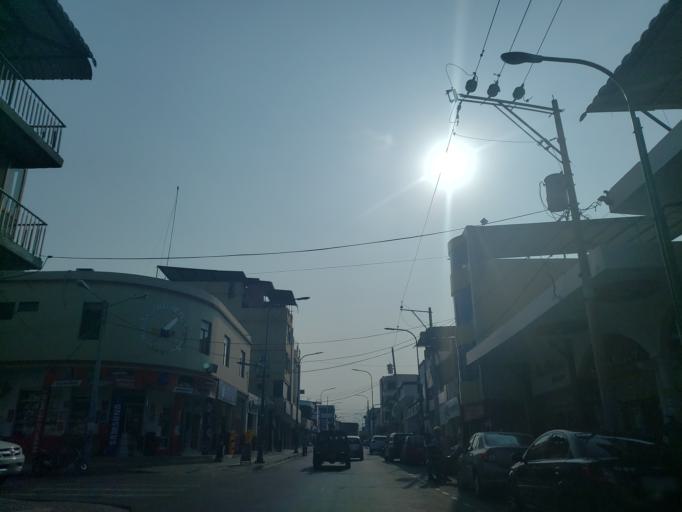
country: EC
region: Manabi
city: Manta
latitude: -0.9475
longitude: -80.7257
